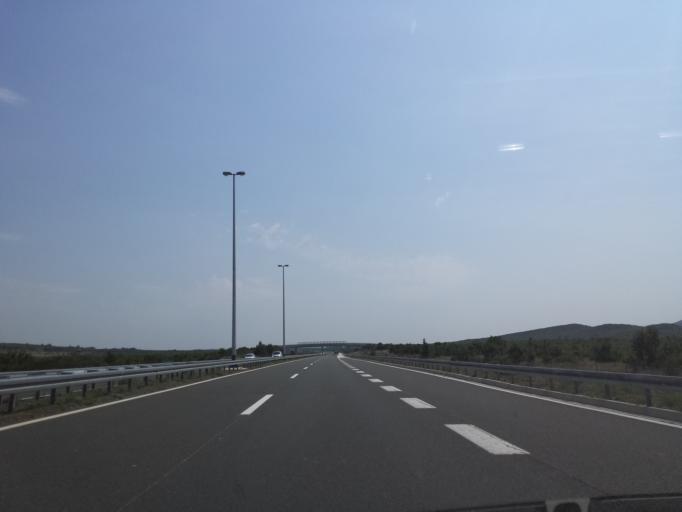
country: HR
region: Zadarska
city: Benkovac
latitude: 43.9431
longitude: 15.6979
